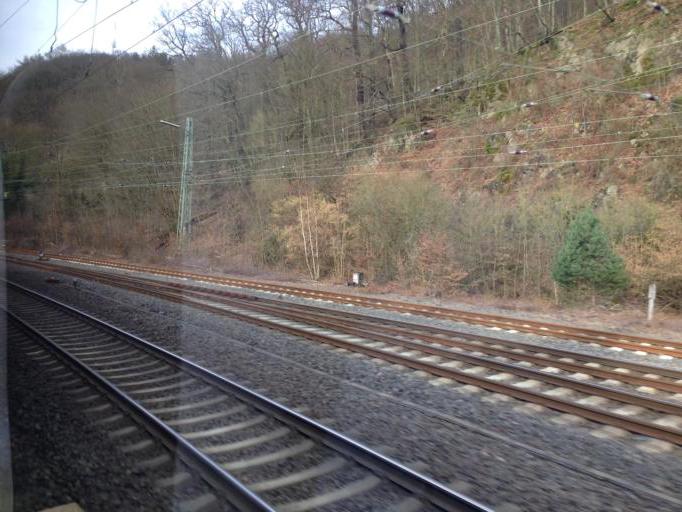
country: DE
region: Hesse
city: Dillenburg
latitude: 50.7393
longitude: 8.2925
